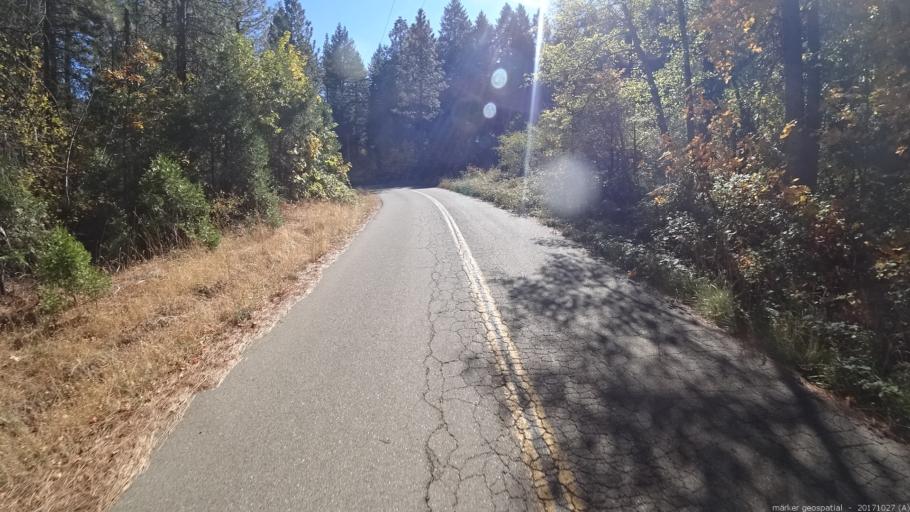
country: US
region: California
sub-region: Shasta County
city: Shingletown
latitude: 40.7381
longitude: -121.9269
